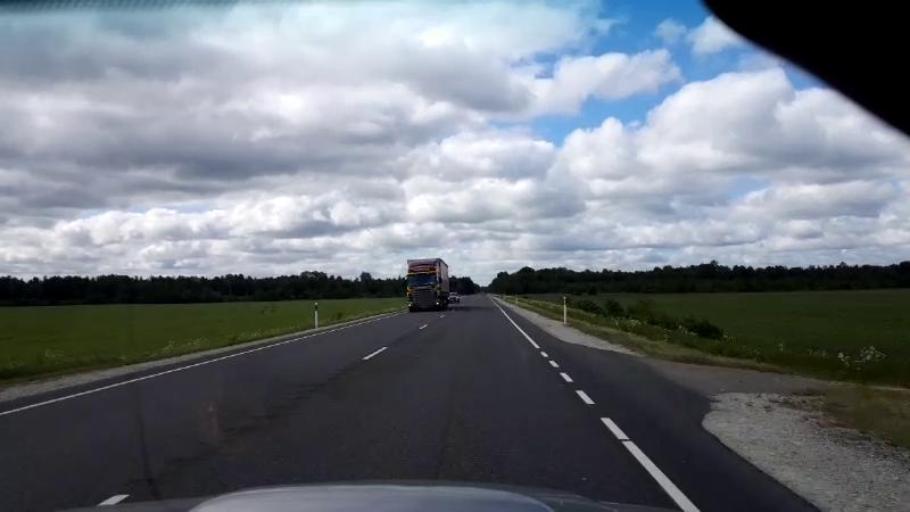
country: EE
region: Raplamaa
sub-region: Maerjamaa vald
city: Marjamaa
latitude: 58.8442
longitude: 24.4262
